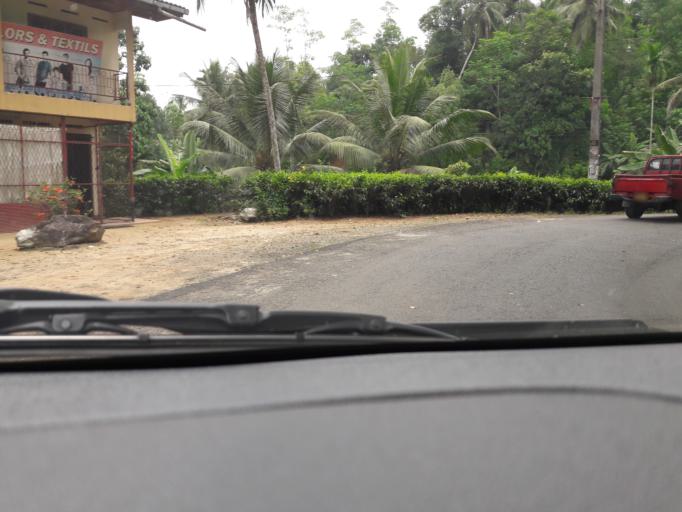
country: LK
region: Southern
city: Galle
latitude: 6.1995
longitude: 80.3017
